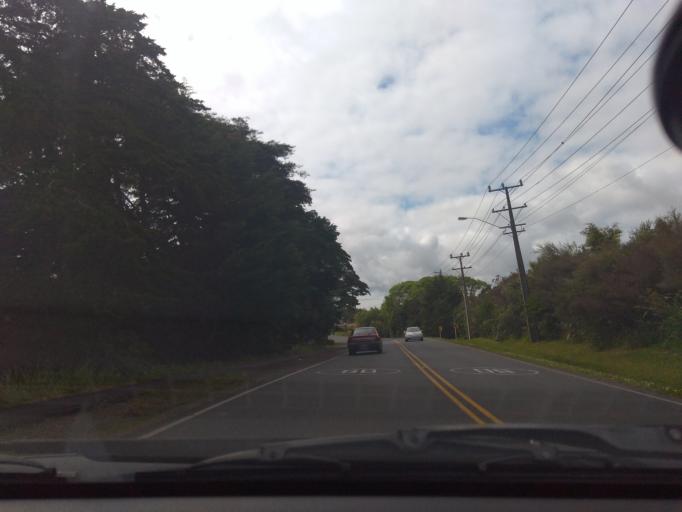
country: NZ
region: Auckland
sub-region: Auckland
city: Rosebank
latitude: -36.8649
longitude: 174.5713
